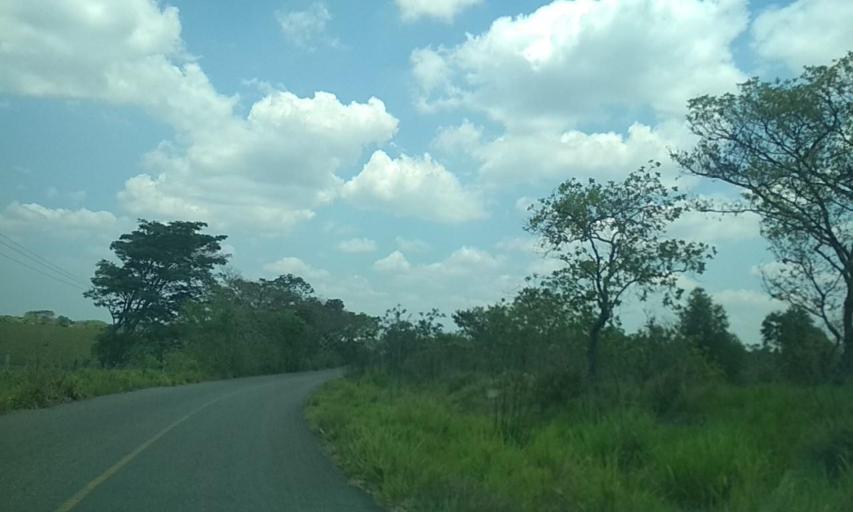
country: MX
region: Tabasco
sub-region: Huimanguillo
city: Francisco Rueda
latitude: 17.7919
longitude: -93.8450
